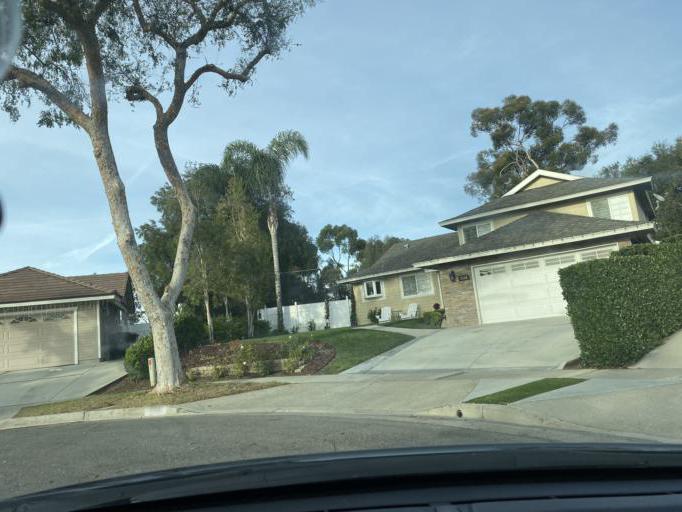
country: US
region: California
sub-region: Orange County
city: Brea
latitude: 33.9003
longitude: -117.8780
